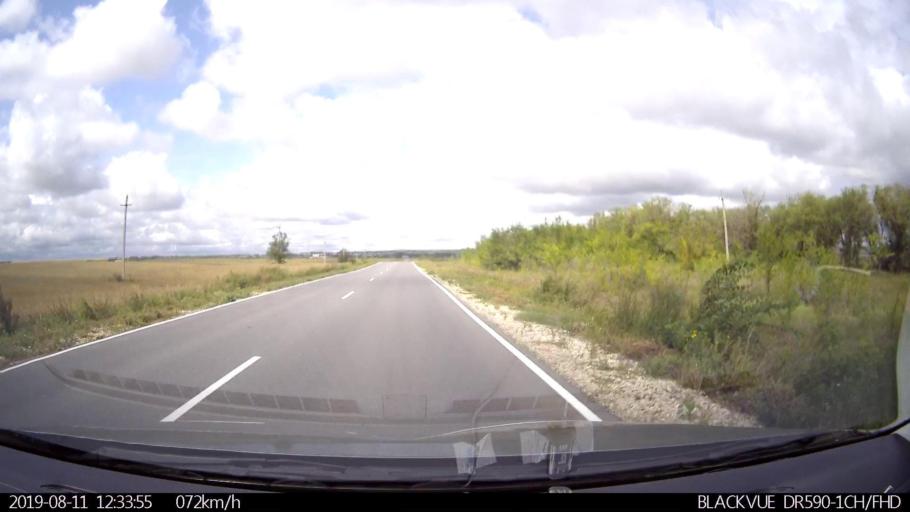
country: RU
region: Ulyanovsk
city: Ignatovka
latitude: 53.8129
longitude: 47.8498
